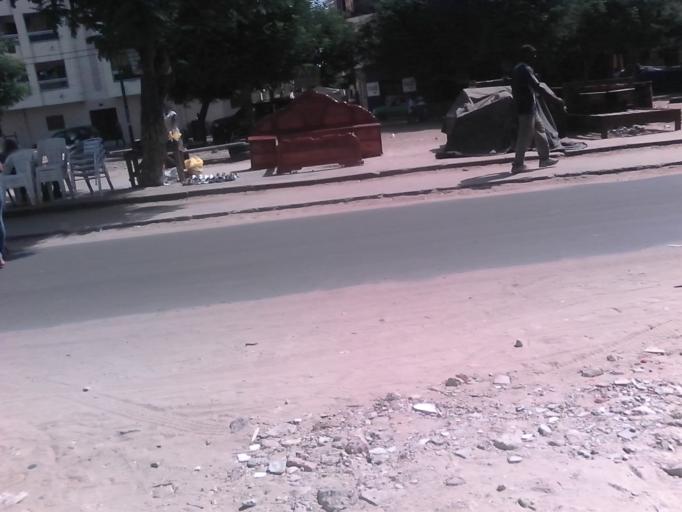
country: SN
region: Dakar
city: Grand Dakar
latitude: 14.7062
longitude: -17.4526
